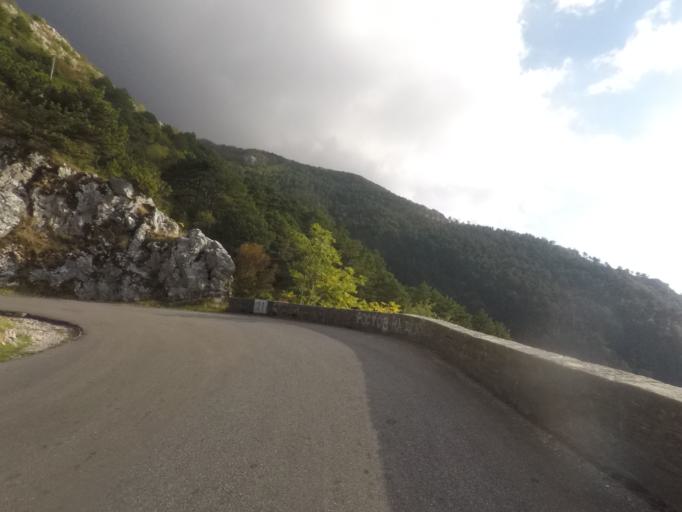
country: ME
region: Kotor
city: Kotor
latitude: 42.4008
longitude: 18.7818
